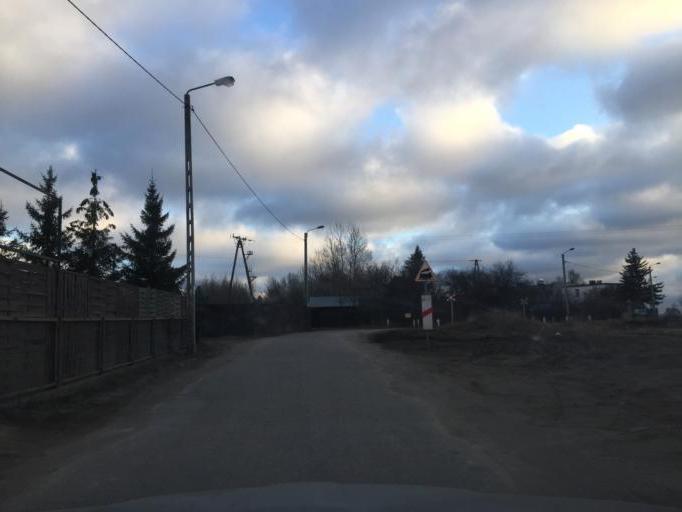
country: PL
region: Pomeranian Voivodeship
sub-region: Powiat kartuski
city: Chwaszczyno
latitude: 54.4161
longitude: 18.4478
